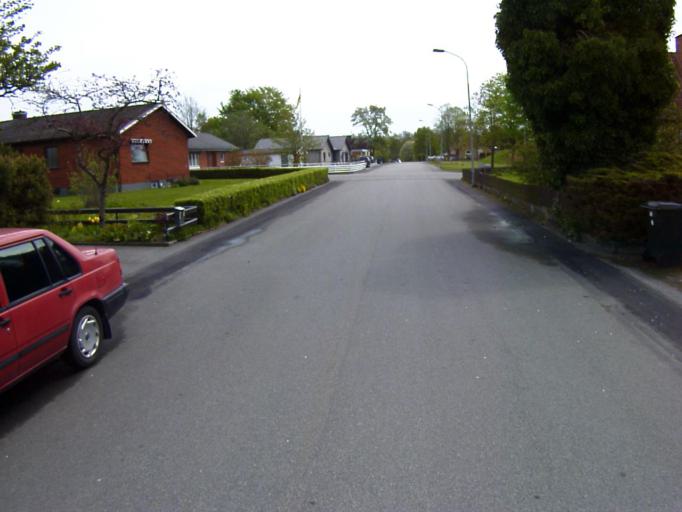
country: SE
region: Skane
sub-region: Kristianstads Kommun
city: Onnestad
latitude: 55.9344
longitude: 13.9854
